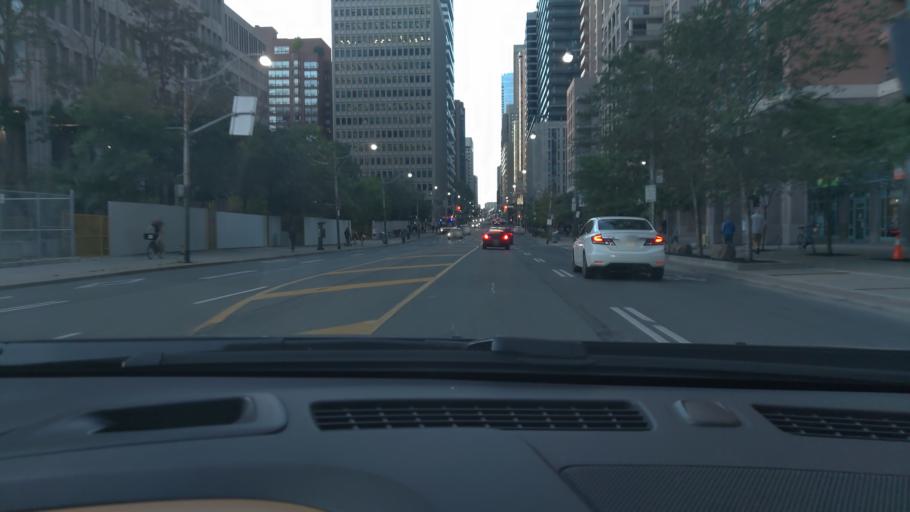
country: CA
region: Ontario
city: Toronto
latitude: 43.6626
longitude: -79.3864
